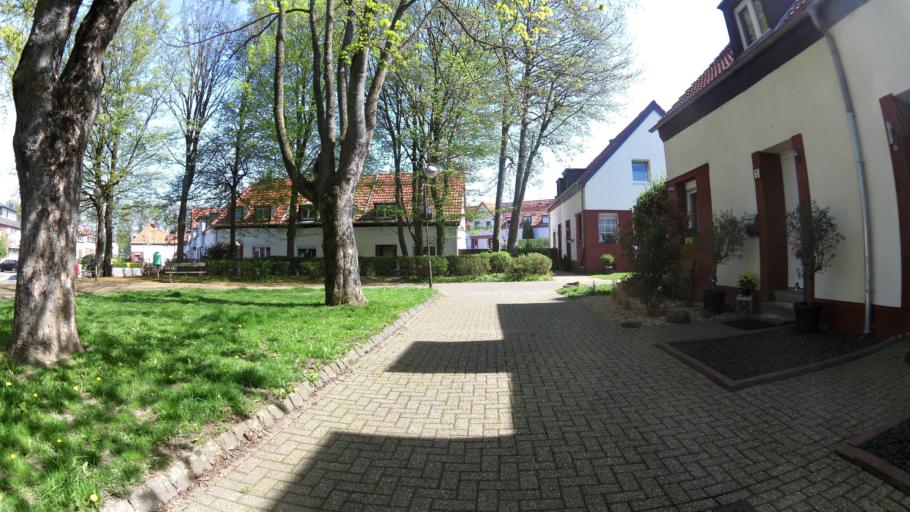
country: DE
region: North Rhine-Westphalia
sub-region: Regierungsbezirk Koln
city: Alsdorf
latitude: 50.8791
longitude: 6.1355
